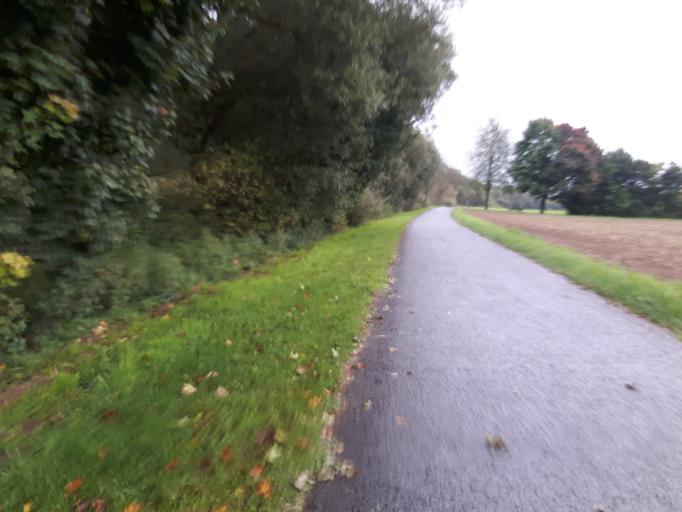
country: DE
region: Bavaria
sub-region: Regierungsbezirk Unterfranken
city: Himmelstadt
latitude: 49.9404
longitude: 9.8005
